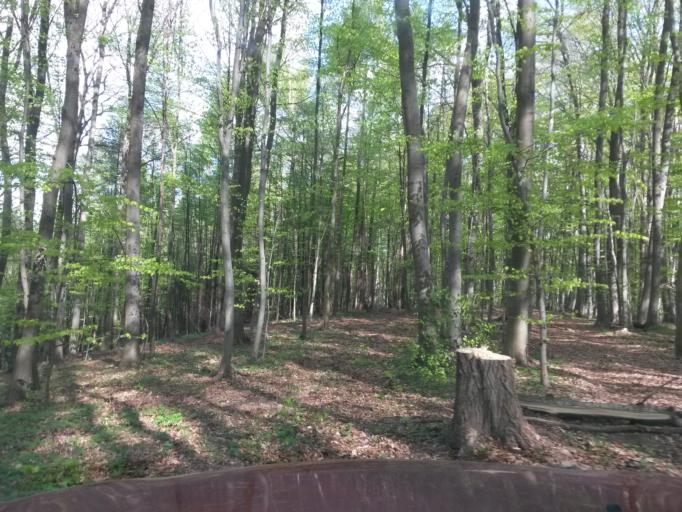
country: SK
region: Presovsky
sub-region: Okres Presov
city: Presov
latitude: 48.9489
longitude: 21.1533
